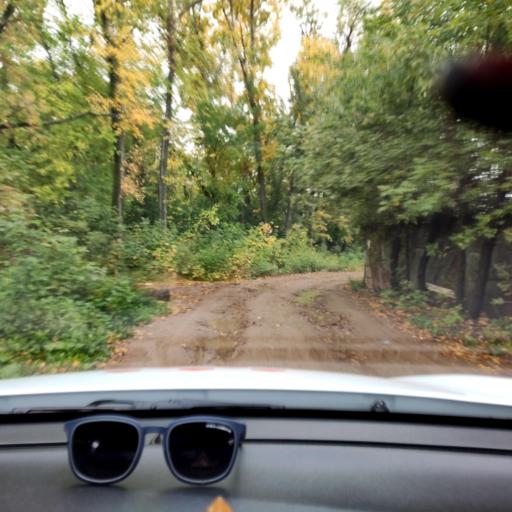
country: RU
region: Tatarstan
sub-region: Gorod Kazan'
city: Kazan
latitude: 55.8099
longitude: 49.1756
